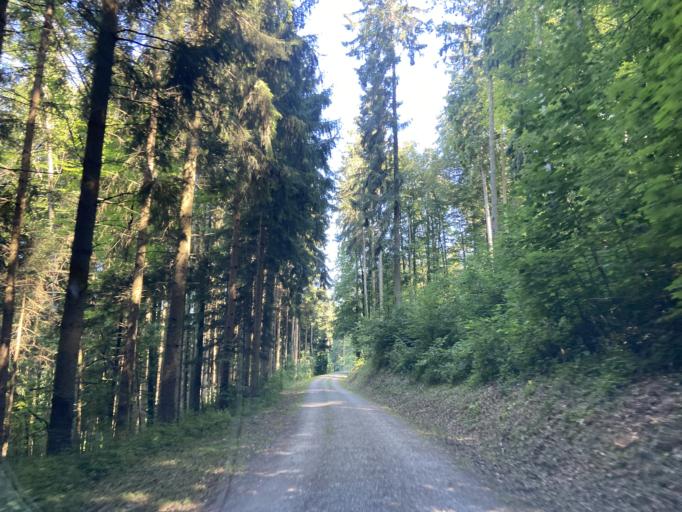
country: CH
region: Zurich
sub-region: Bezirk Winterthur
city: Wuelflingen (Kreis 6) / Niederfeld
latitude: 47.5048
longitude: 8.6663
